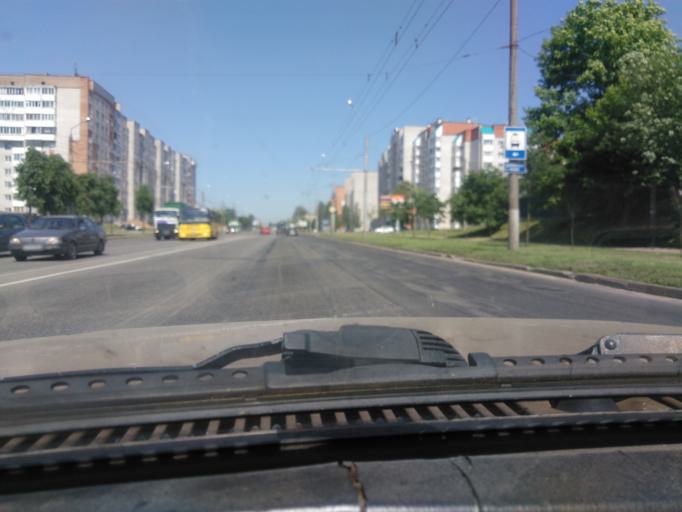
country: BY
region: Mogilev
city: Mahilyow
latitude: 53.9319
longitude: 30.3520
